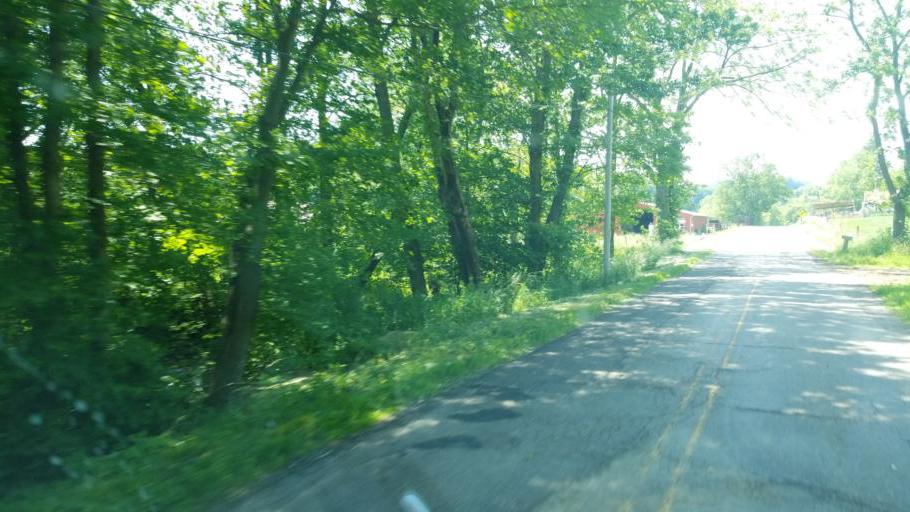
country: US
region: Ohio
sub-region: Knox County
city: Danville
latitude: 40.5034
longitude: -82.3574
